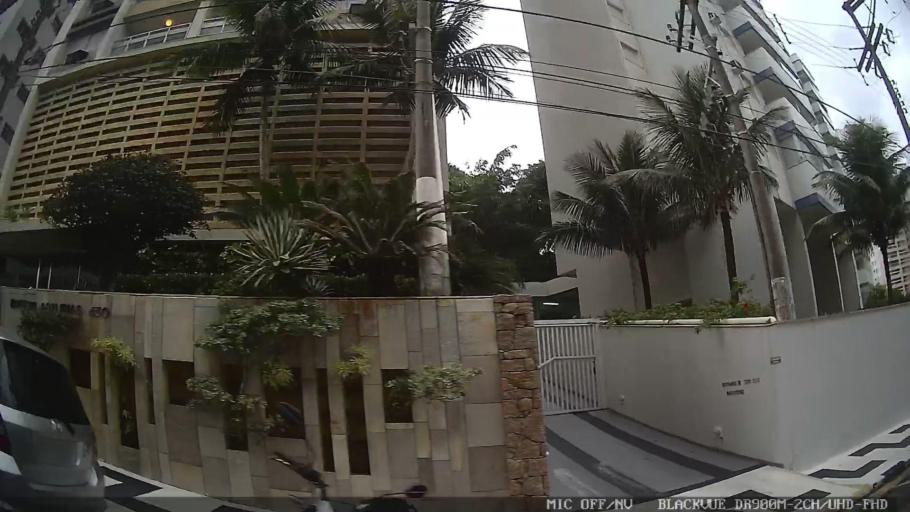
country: BR
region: Sao Paulo
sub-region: Guaruja
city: Guaruja
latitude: -24.0128
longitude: -46.2647
